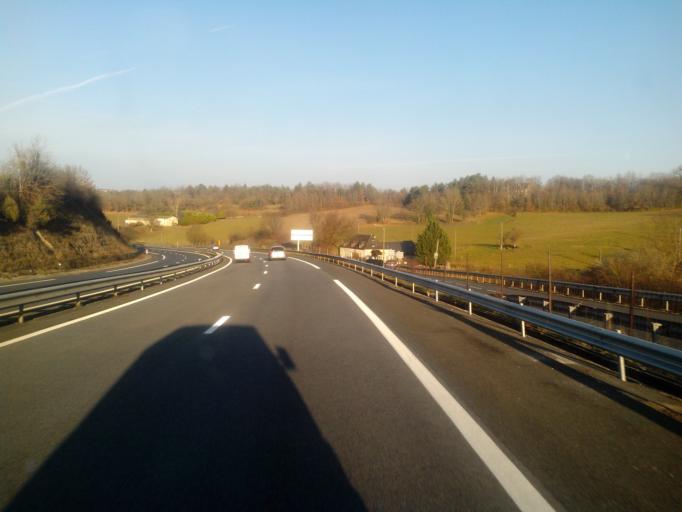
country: FR
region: Limousin
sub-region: Departement de la Correze
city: Brive-la-Gaillarde
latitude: 45.0855
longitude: 1.5167
